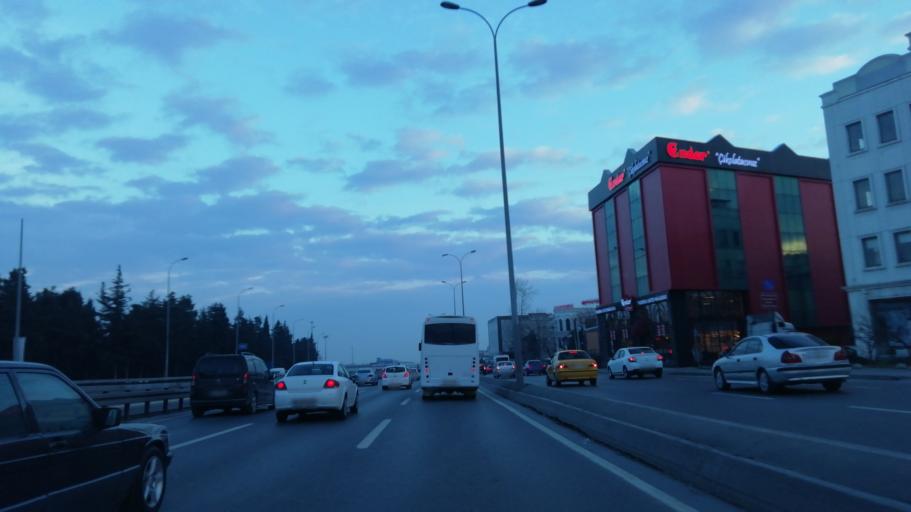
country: TR
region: Istanbul
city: Yakuplu
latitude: 40.9878
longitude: 28.7184
